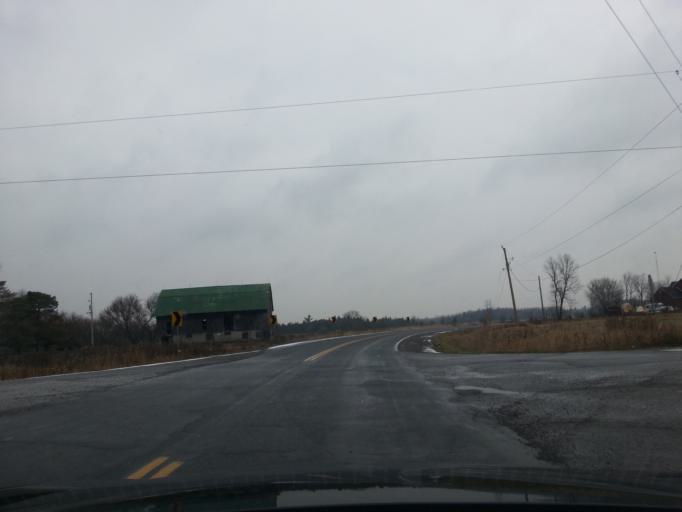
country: CA
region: Ontario
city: Carleton Place
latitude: 45.1008
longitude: -76.0316
